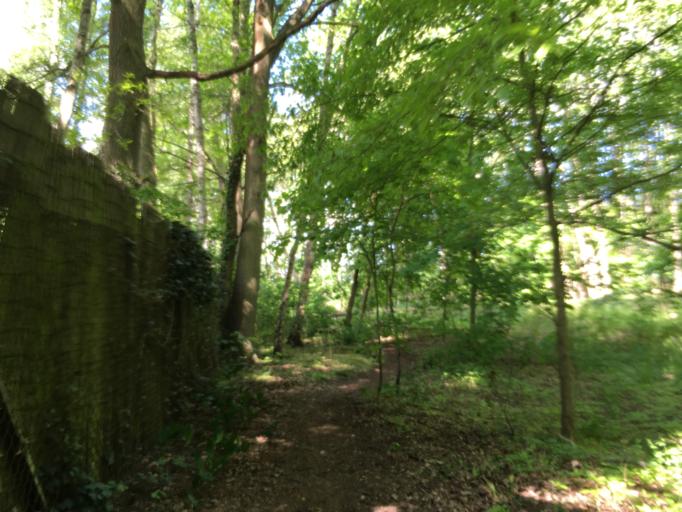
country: DE
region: Berlin
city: Blankenfelde
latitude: 52.6518
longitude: 13.3799
